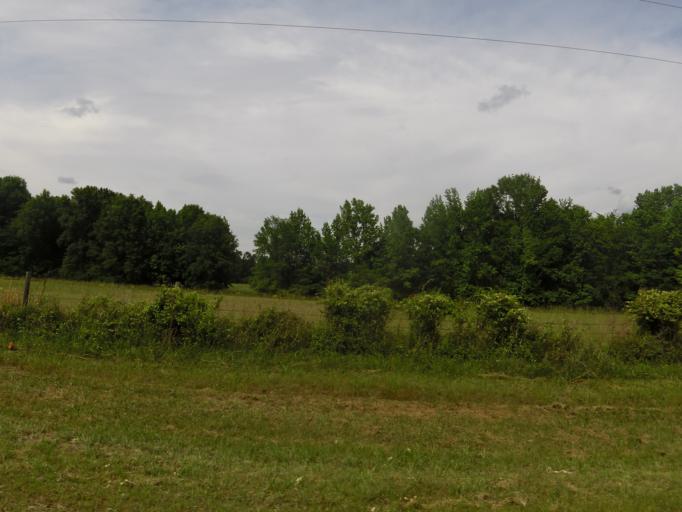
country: US
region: Georgia
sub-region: McDuffie County
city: Thomson
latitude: 33.5368
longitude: -82.4970
